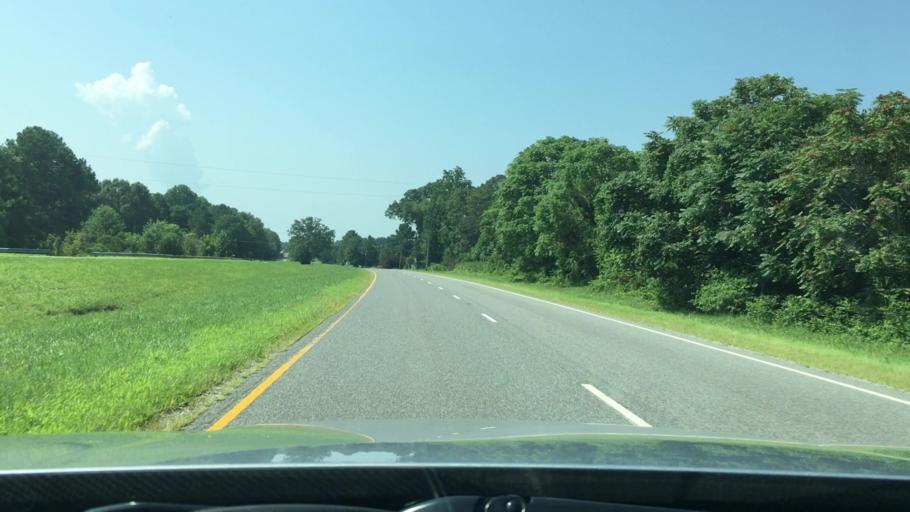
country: US
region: Virginia
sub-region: Caroline County
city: Bowling Green
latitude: 38.0125
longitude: -77.4123
